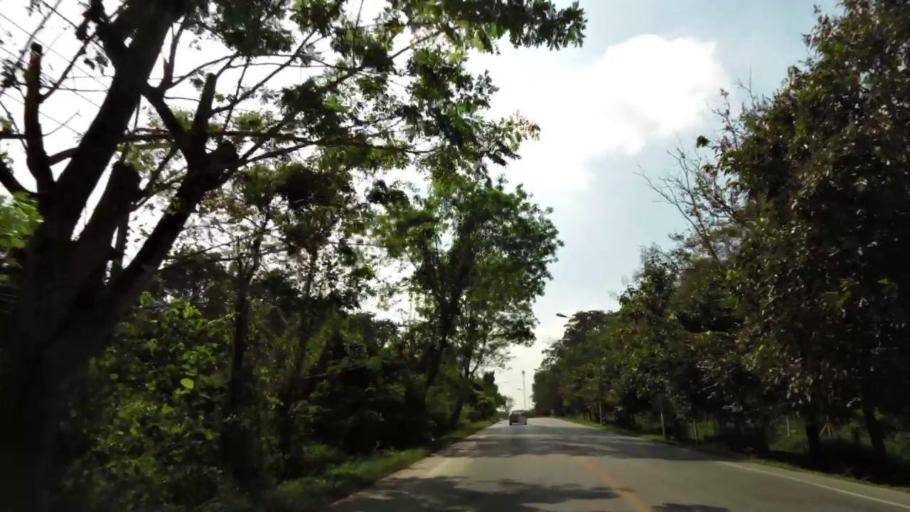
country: TH
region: Chiang Rai
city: Chiang Rai
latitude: 19.8711
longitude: 99.7799
